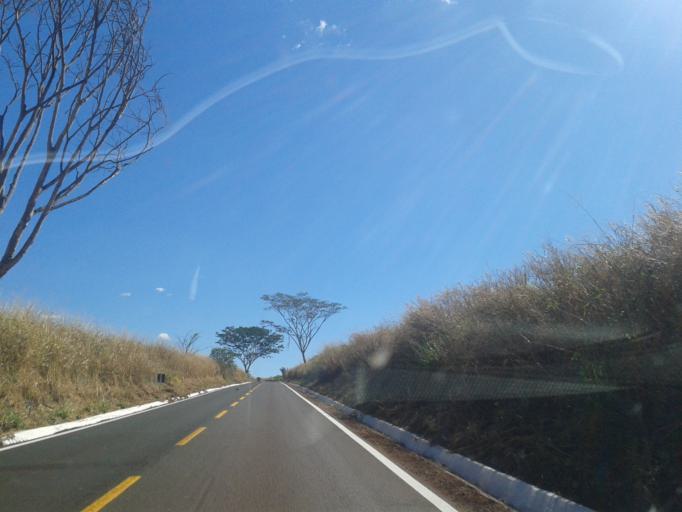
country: BR
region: Minas Gerais
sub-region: Capinopolis
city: Capinopolis
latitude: -18.6916
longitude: -49.4600
